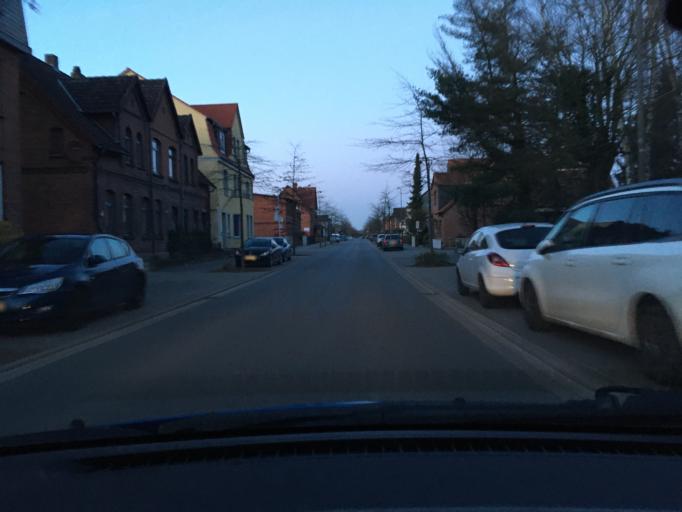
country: DE
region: Lower Saxony
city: Uelzen
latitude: 52.9741
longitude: 10.5658
